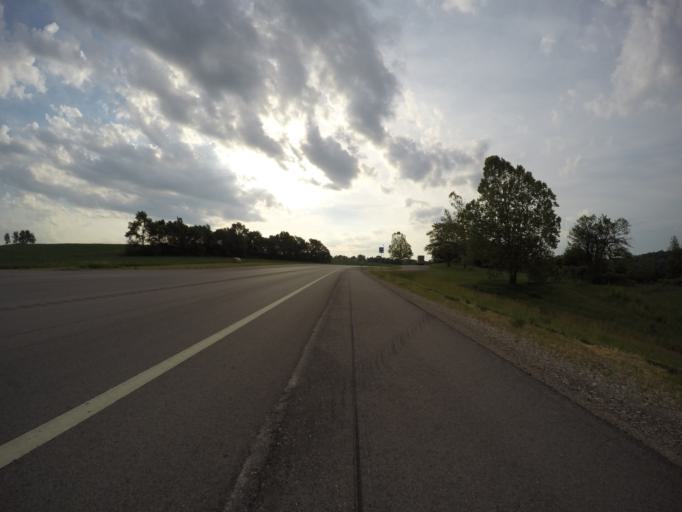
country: US
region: Kansas
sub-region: Doniphan County
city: Troy
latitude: 39.7935
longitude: -95.0548
